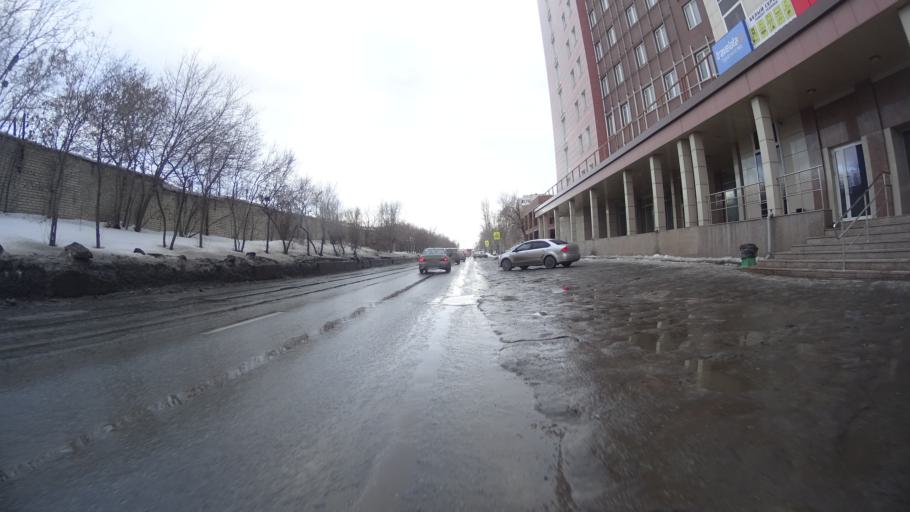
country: RU
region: Chelyabinsk
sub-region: Gorod Chelyabinsk
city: Chelyabinsk
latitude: 55.1426
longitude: 61.4010
